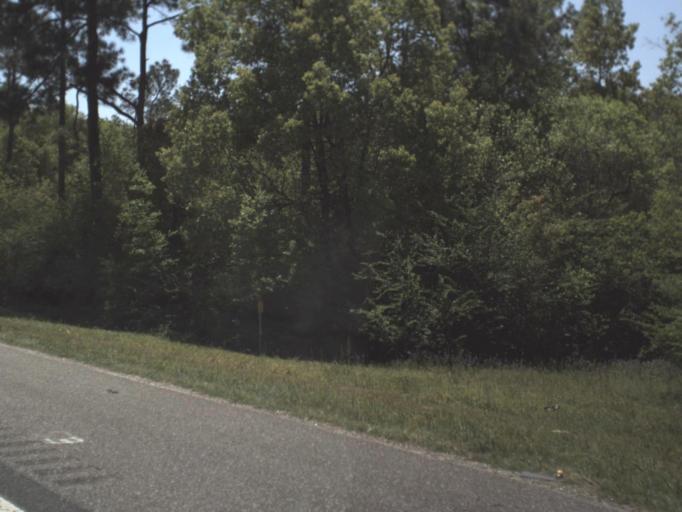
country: US
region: Florida
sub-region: Escambia County
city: Ensley
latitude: 30.5171
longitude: -87.3058
